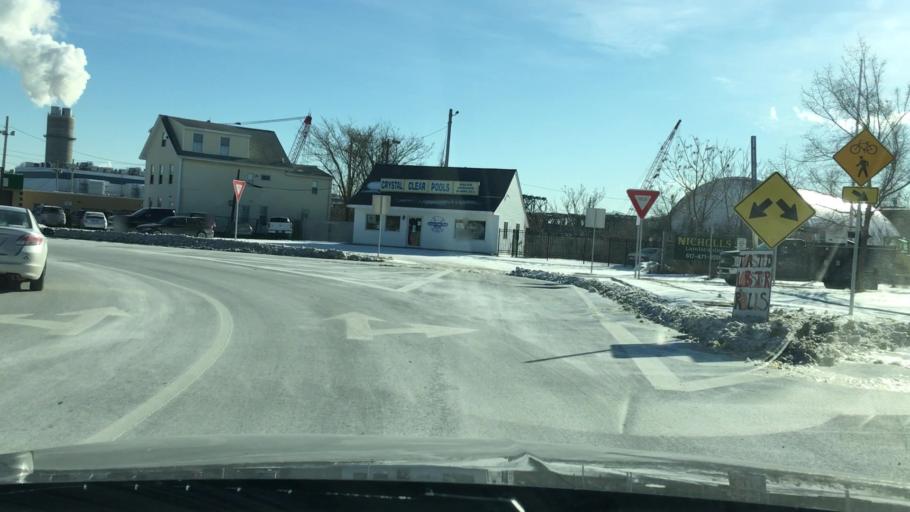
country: US
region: Massachusetts
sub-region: Norfolk County
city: Quincy
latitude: 42.2454
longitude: -70.9726
